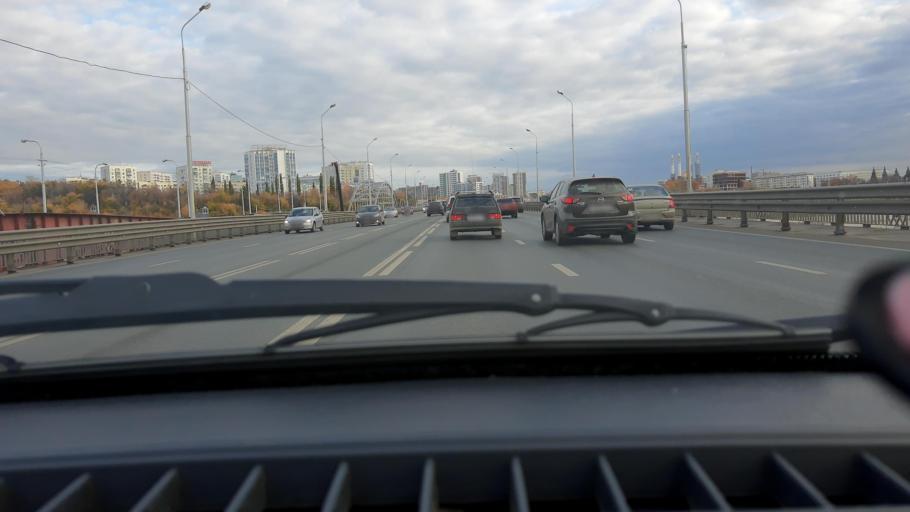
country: RU
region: Bashkortostan
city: Ufa
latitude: 54.7047
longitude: 55.9542
